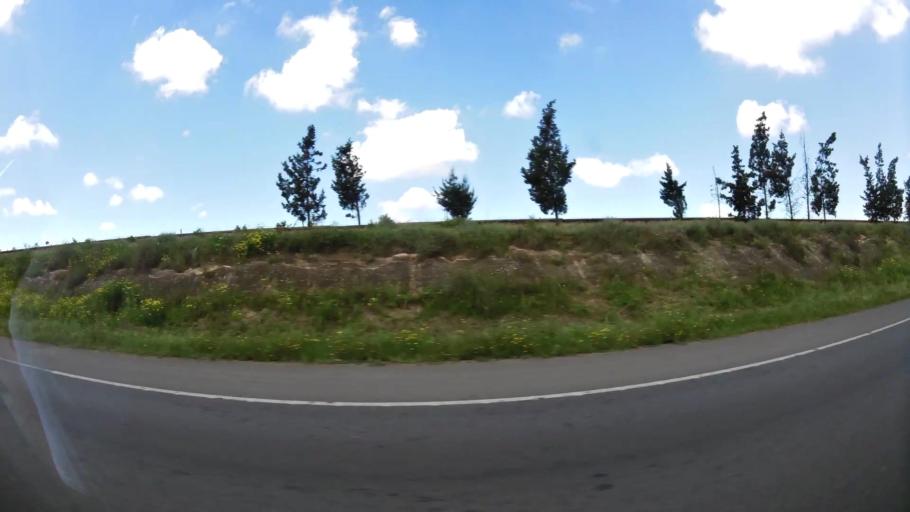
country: MA
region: Grand Casablanca
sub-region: Casablanca
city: Casablanca
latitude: 33.5178
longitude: -7.5854
